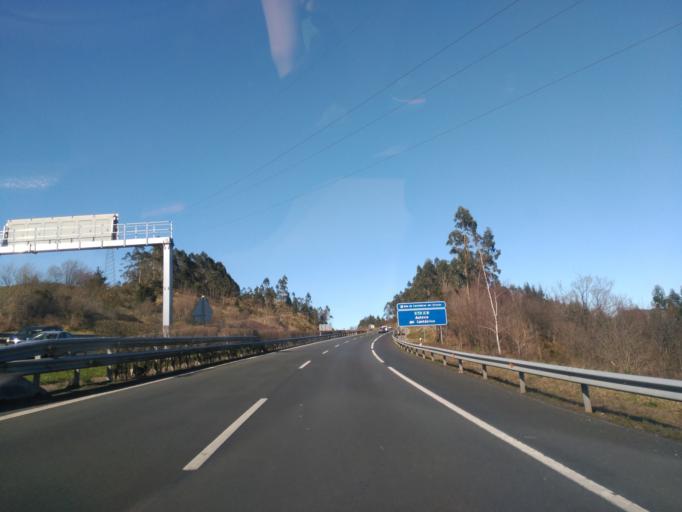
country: ES
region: Cantabria
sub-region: Provincia de Cantabria
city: Cabezon de la Sal
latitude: 43.3178
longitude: -4.2653
